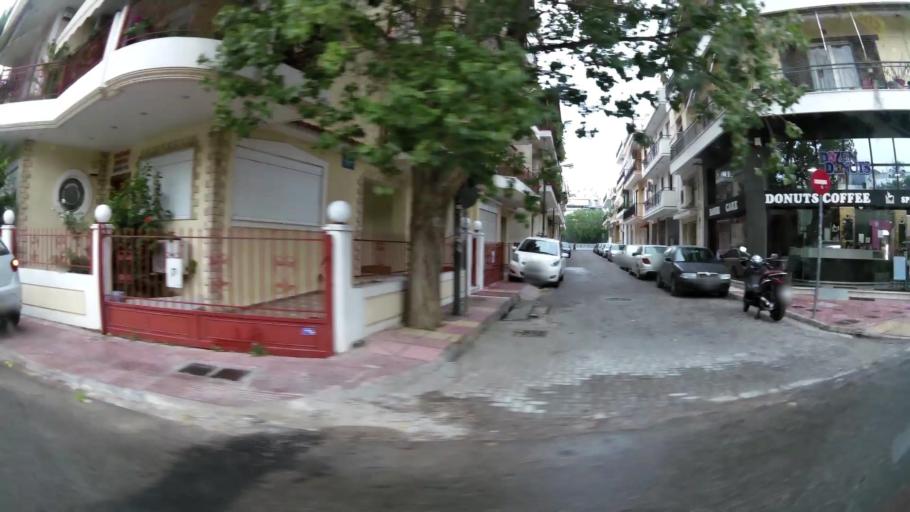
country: GR
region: Attica
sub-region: Nomarchia Athinas
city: Nea Filadelfeia
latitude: 38.0401
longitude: 23.7288
